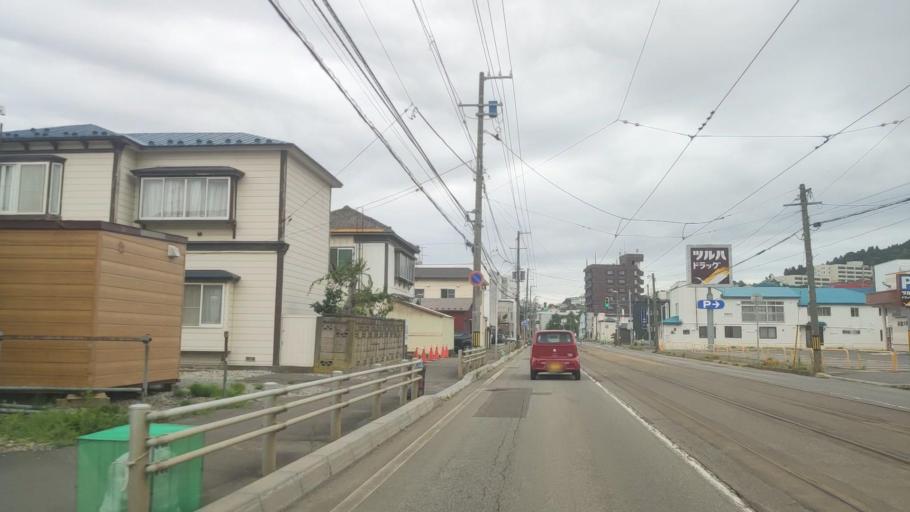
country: JP
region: Hokkaido
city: Hakodate
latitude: 41.7694
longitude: 140.7098
